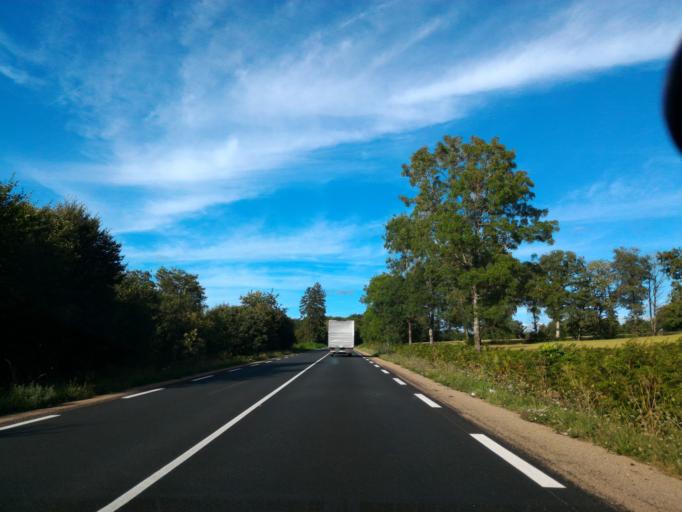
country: FR
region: Limousin
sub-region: Departement de la Haute-Vienne
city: Magnac-Laval
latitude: 46.1779
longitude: 1.1563
